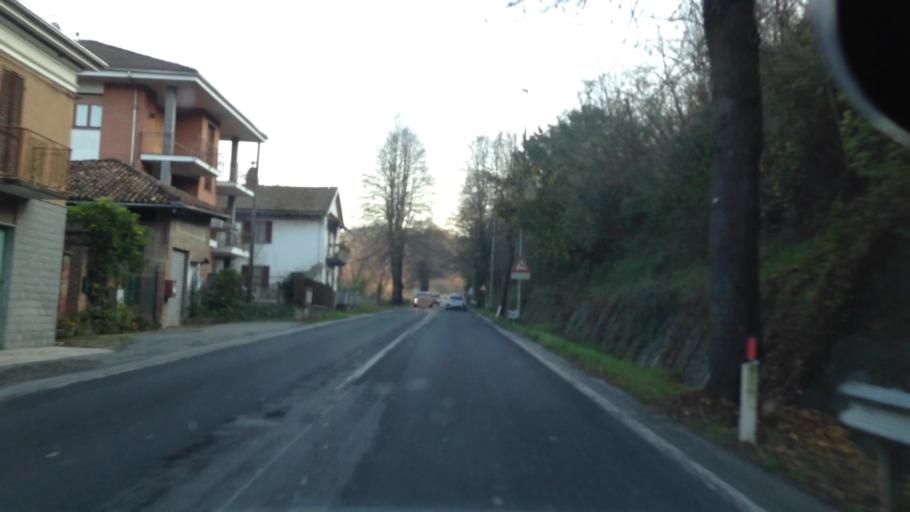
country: IT
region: Piedmont
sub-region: Provincia di Torino
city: Cavagnolo
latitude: 45.1323
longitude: 8.0571
